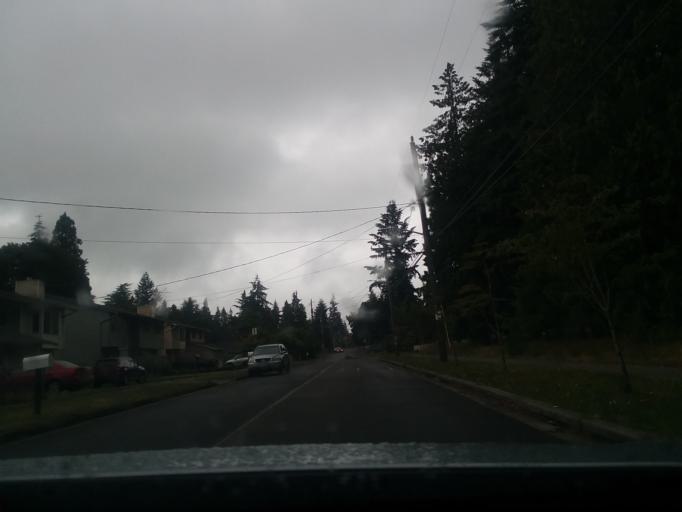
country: US
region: Washington
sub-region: King County
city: Shoreline
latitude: 47.7262
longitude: -122.3396
